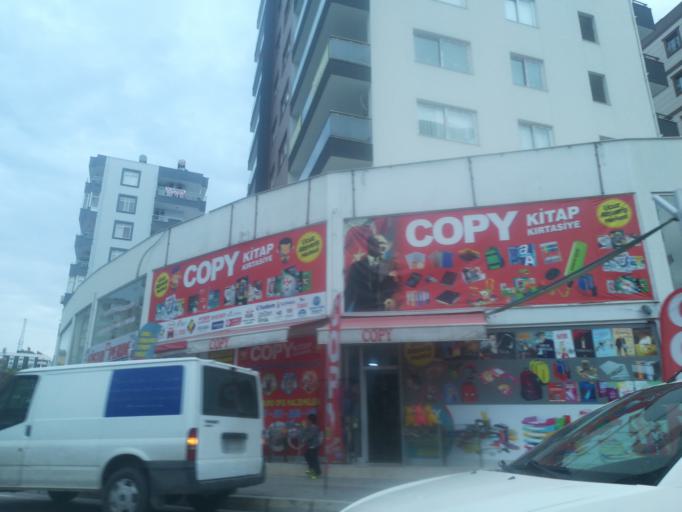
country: TR
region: Adana
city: Adana
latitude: 37.0444
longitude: 35.2911
